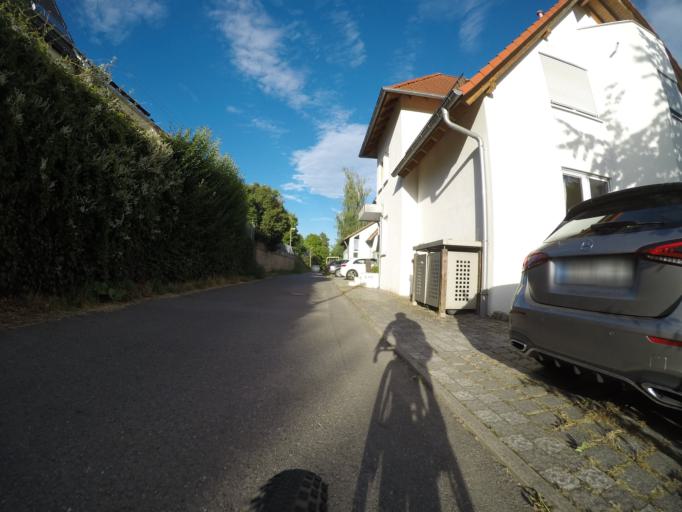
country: DE
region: Baden-Wuerttemberg
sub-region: Regierungsbezirk Stuttgart
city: Ehningen
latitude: 48.6918
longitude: 8.9564
